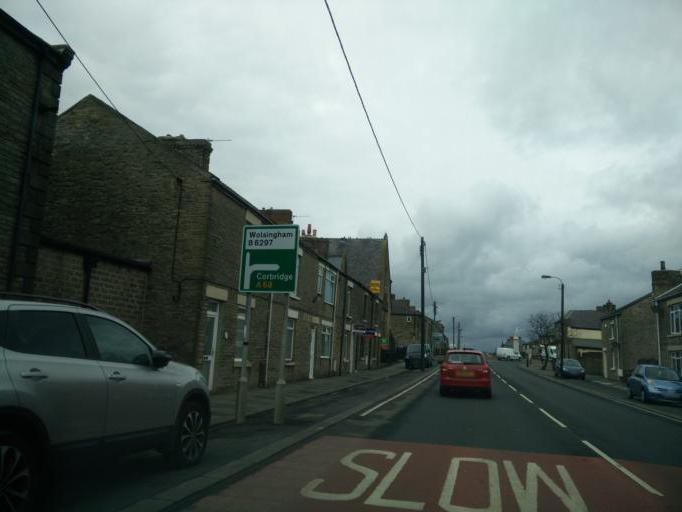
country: GB
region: England
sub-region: County Durham
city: Tow Law
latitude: 54.7420
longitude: -1.8128
